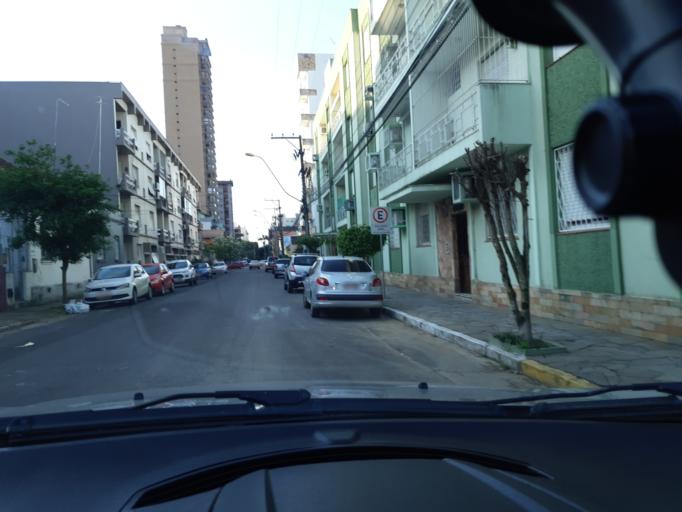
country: BR
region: Rio Grande do Sul
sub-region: Sao Leopoldo
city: Sao Leopoldo
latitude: -29.7652
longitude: -51.1418
